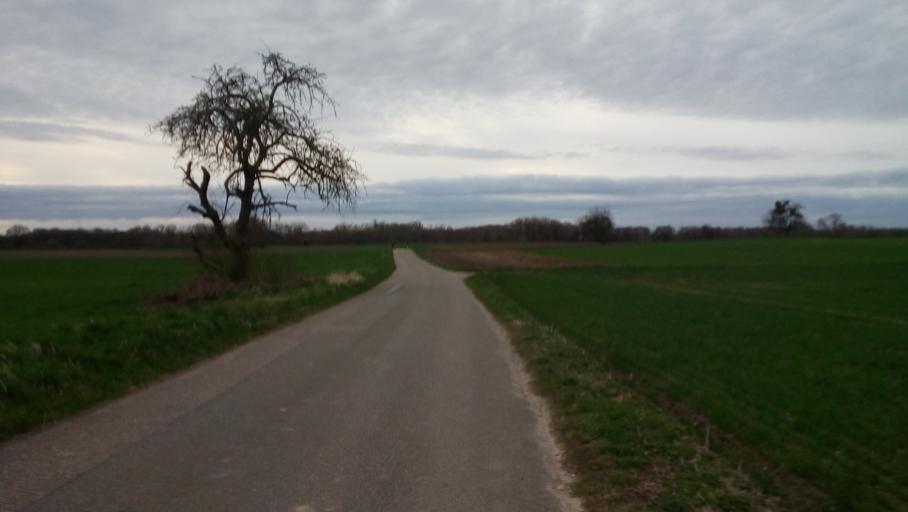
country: DE
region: Baden-Wuerttemberg
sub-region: Karlsruhe Region
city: Lichtenau
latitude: 48.7124
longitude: 7.9857
